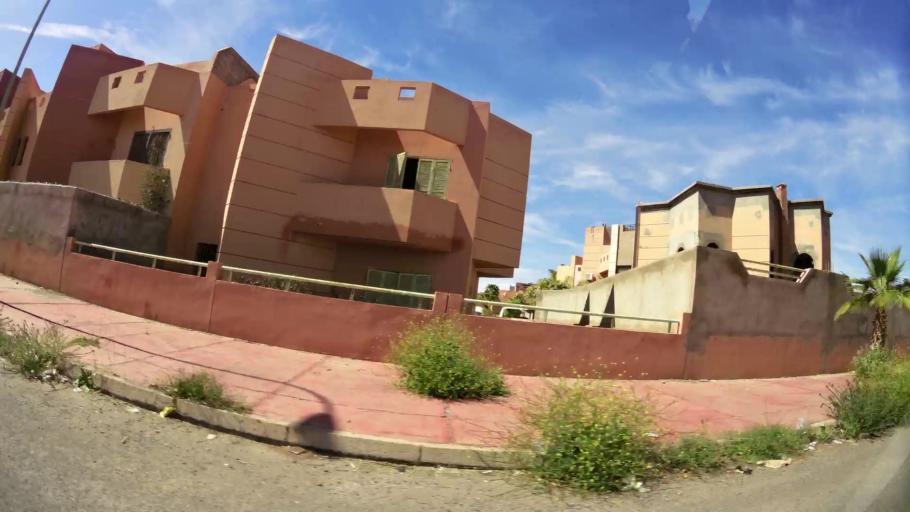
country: MA
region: Marrakech-Tensift-Al Haouz
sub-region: Marrakech
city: Marrakesh
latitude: 31.6366
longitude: -8.1066
